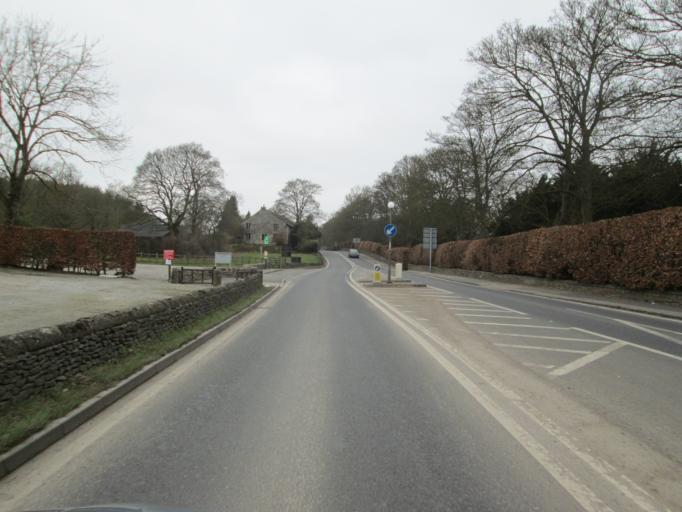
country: GB
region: England
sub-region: Derbyshire
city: Bakewell
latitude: 53.1919
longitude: -1.6514
